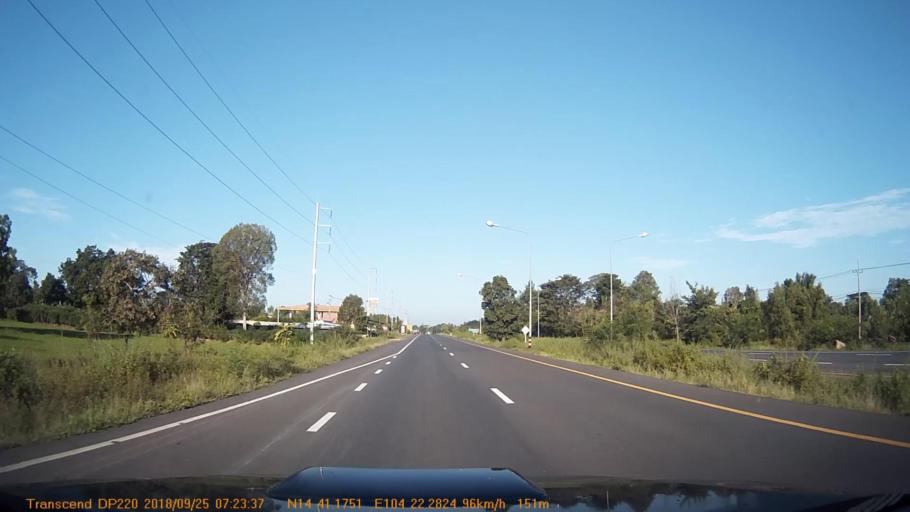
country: TH
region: Sisaket
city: Phrai Bueng
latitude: 14.6863
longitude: 104.3707
